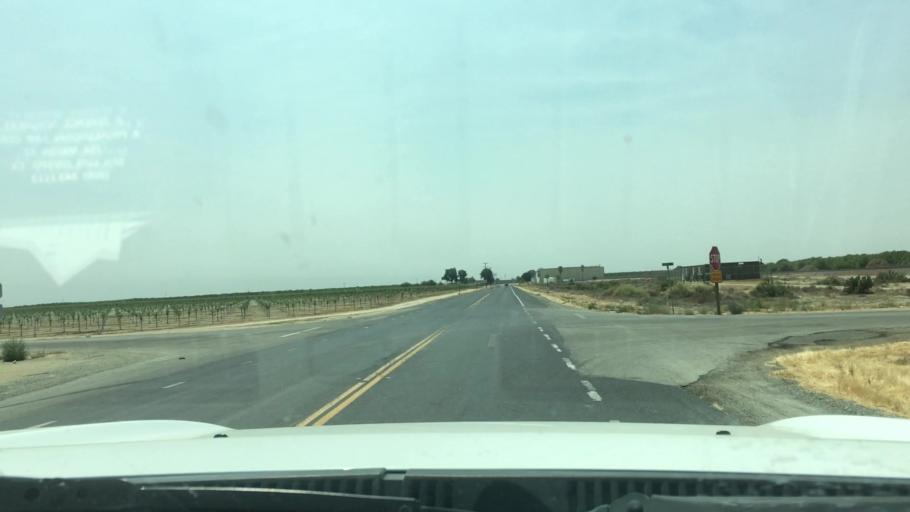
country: US
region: California
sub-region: Kern County
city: Delano
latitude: 35.7615
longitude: -119.3446
